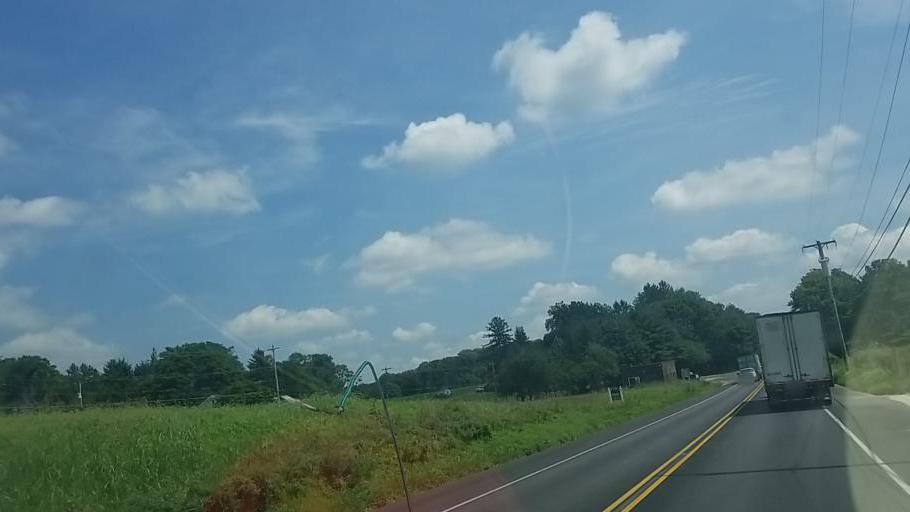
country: US
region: Delaware
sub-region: New Castle County
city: Hockessin
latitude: 39.7995
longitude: -75.7297
